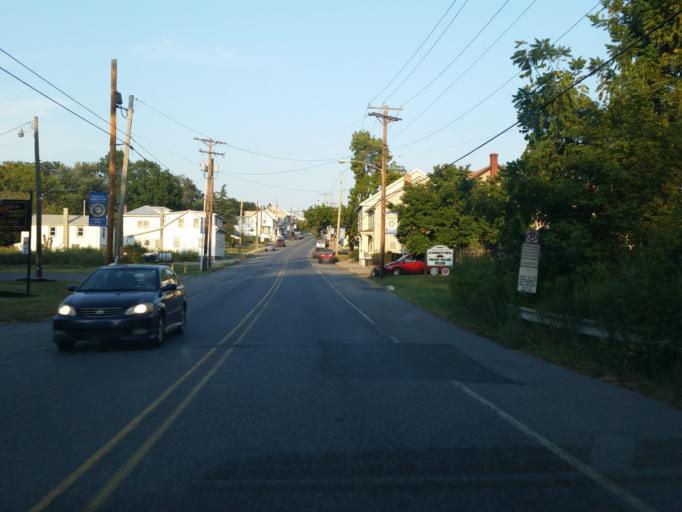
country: US
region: Pennsylvania
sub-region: Lebanon County
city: Jonestown
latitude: 40.4128
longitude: -76.4860
